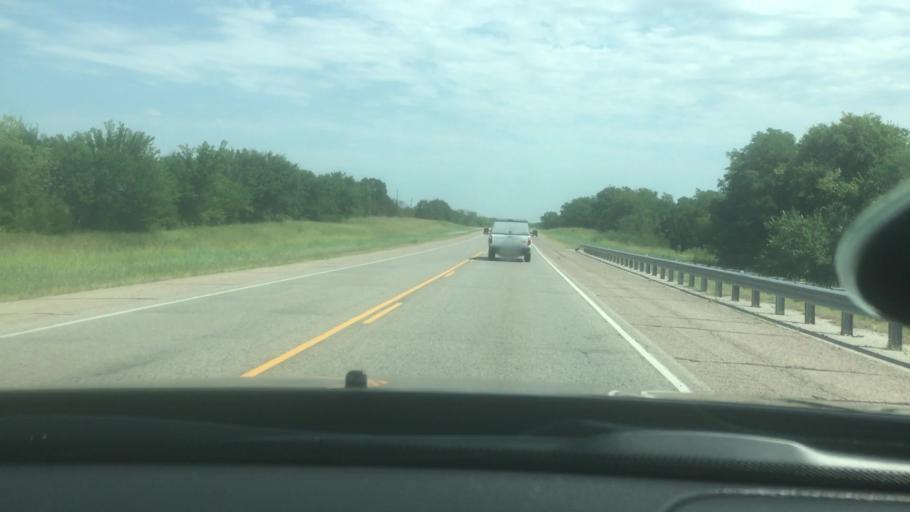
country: US
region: Oklahoma
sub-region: Seminole County
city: Maud
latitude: 35.0447
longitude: -96.9315
